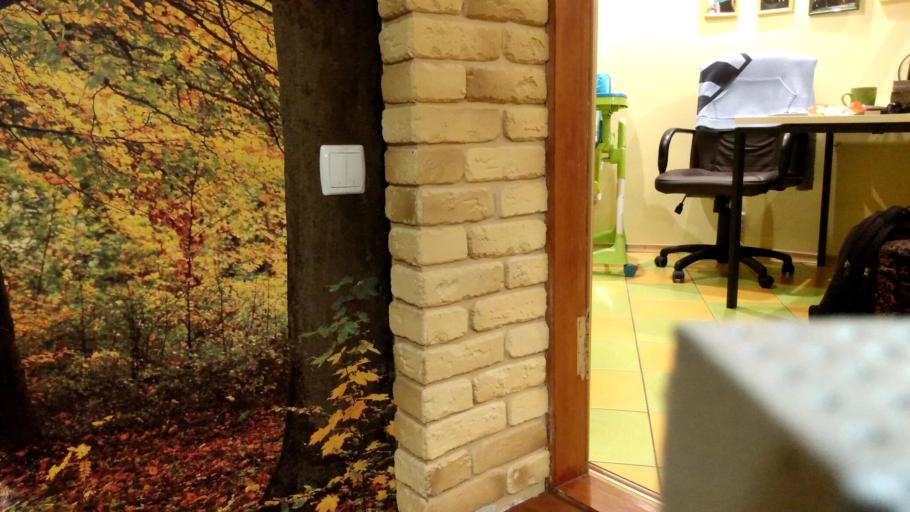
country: RU
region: Republic of Karelia
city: Pudozh
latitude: 61.6638
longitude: 37.7210
